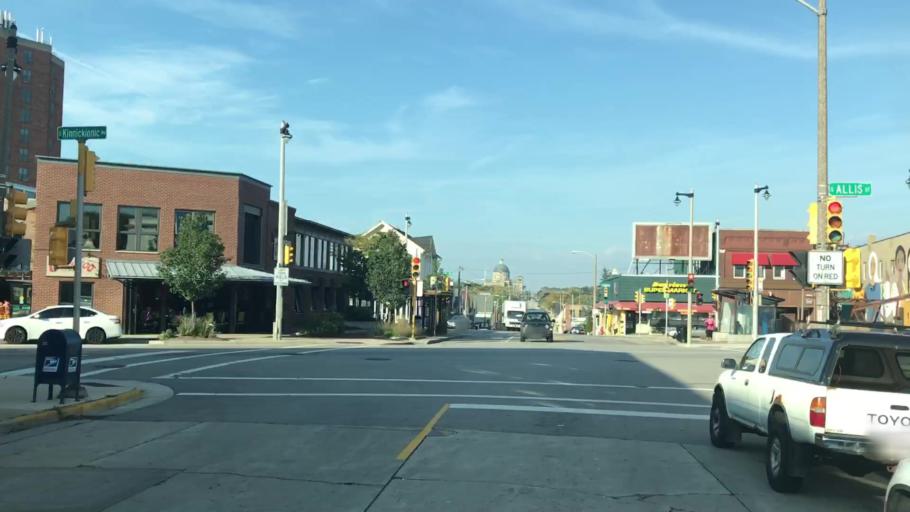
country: US
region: Wisconsin
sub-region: Milwaukee County
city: Milwaukee
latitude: 43.0029
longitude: -87.9037
